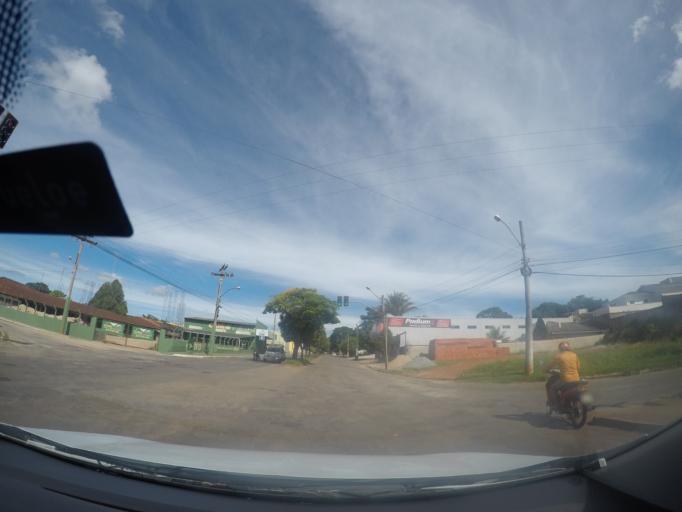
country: BR
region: Goias
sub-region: Inhumas
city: Inhumas
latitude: -16.3666
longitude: -49.4978
